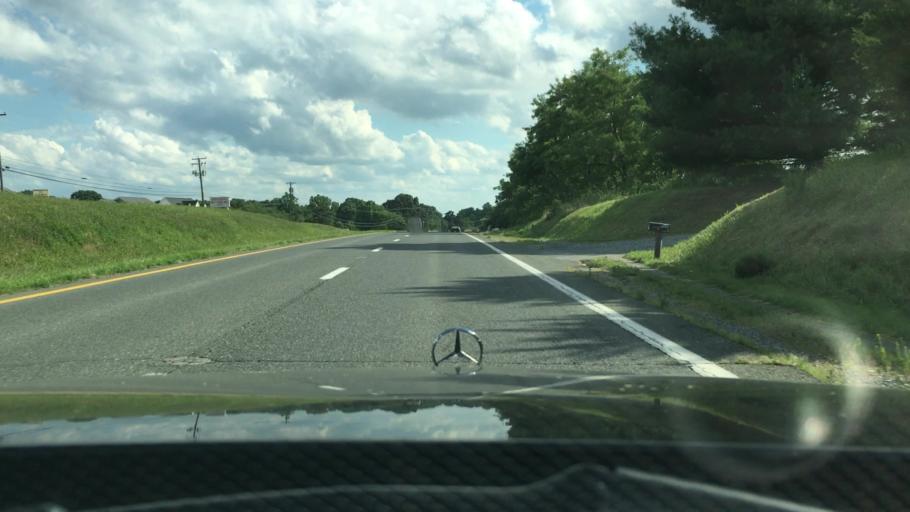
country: US
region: Virginia
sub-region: Campbell County
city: Altavista
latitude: 37.1715
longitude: -79.2093
